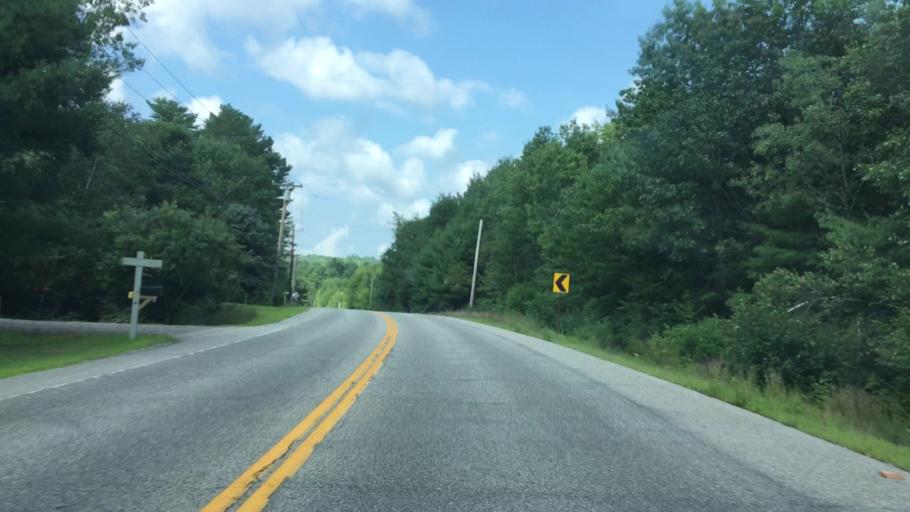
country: US
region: Maine
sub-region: Androscoggin County
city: Minot
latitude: 44.0301
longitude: -70.3382
